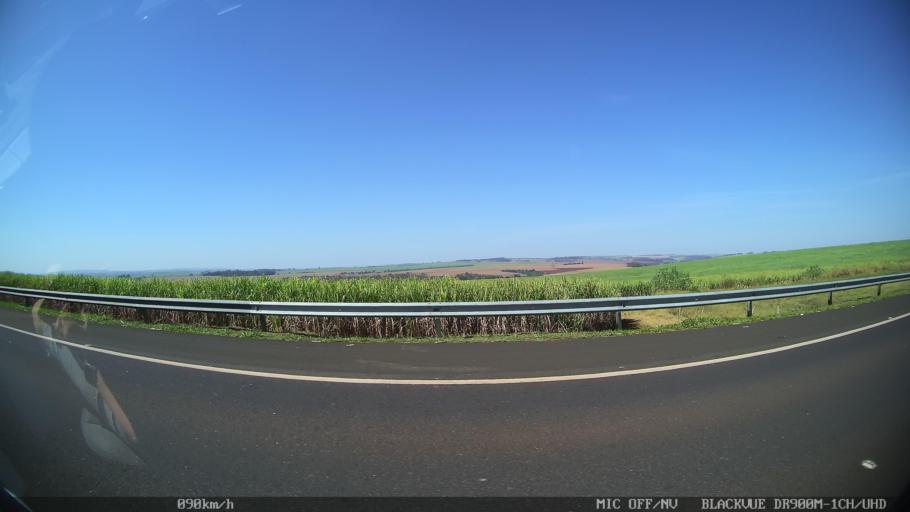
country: BR
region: Sao Paulo
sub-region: Batatais
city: Batatais
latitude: -20.7712
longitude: -47.5409
